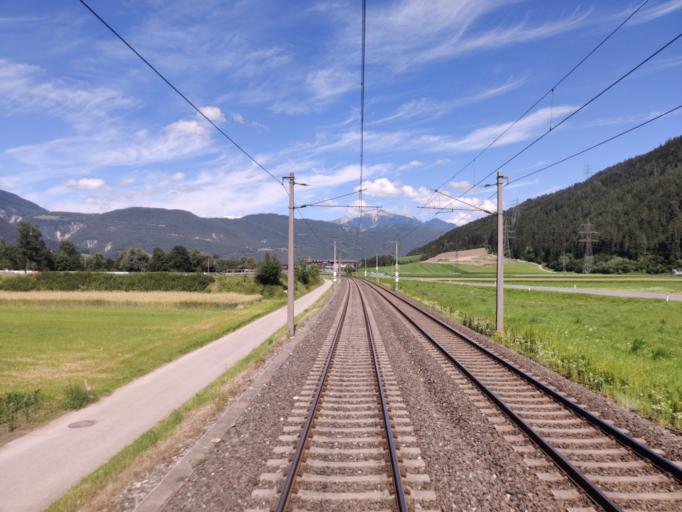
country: AT
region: Tyrol
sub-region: Politischer Bezirk Imst
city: Rietz
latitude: 47.2941
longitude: 11.0509
